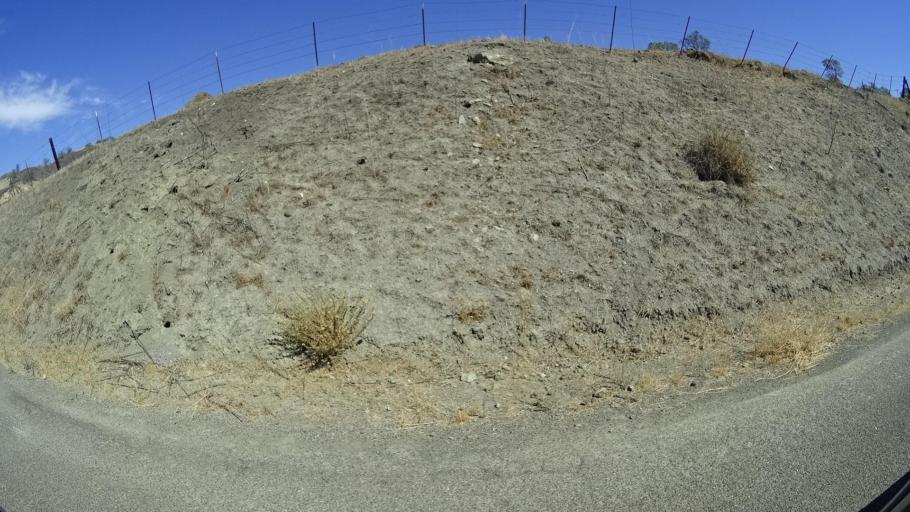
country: US
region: California
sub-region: Fresno County
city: Coalinga
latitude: 36.0974
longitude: -120.6881
